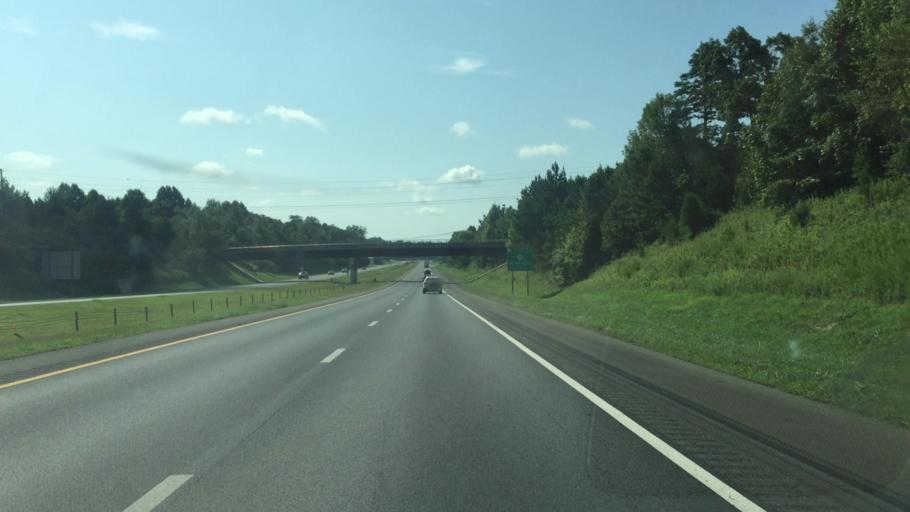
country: US
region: North Carolina
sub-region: Mecklenburg County
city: Mint Hill
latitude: 35.2098
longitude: -80.6414
